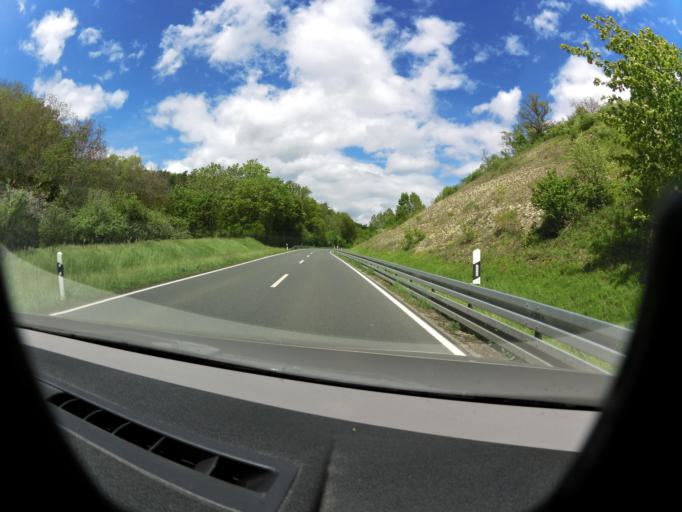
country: DE
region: Bavaria
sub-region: Regierungsbezirk Unterfranken
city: Frickenhausen
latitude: 49.6745
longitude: 10.0793
